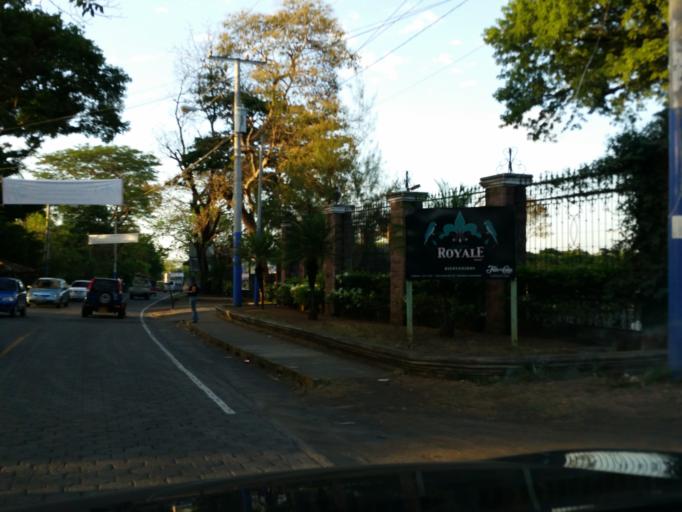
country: NI
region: Masaya
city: Ticuantepe
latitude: 12.0348
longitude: -86.2055
